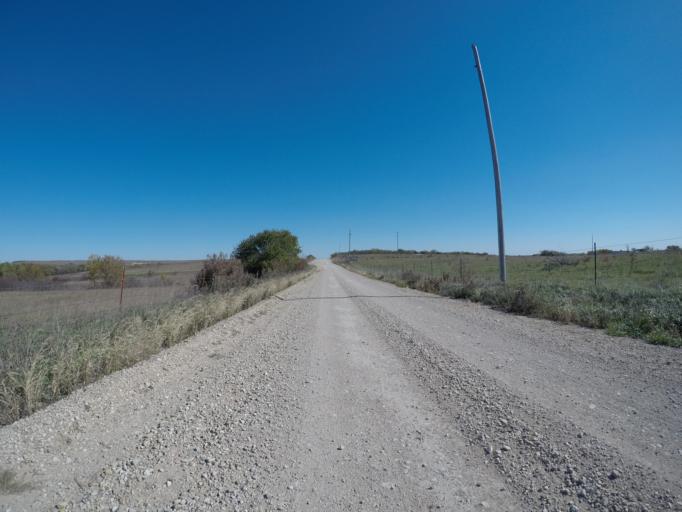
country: US
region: Kansas
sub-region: Wabaunsee County
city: Alma
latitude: 39.0580
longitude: -96.3547
